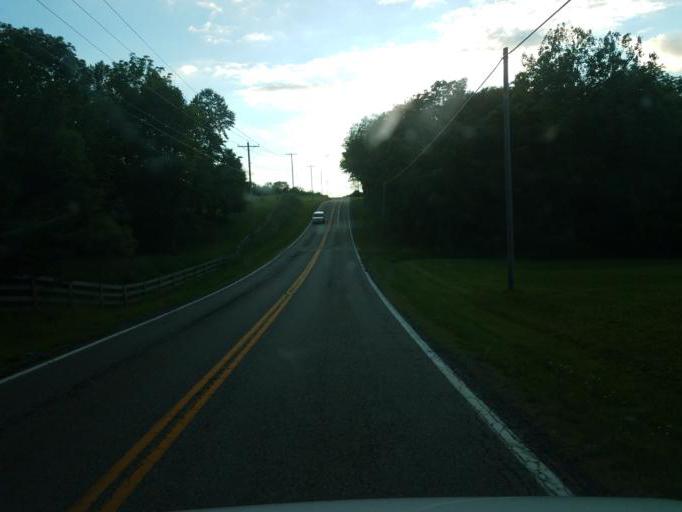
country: US
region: Ohio
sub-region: Knox County
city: Fredericktown
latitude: 40.4023
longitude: -82.6086
